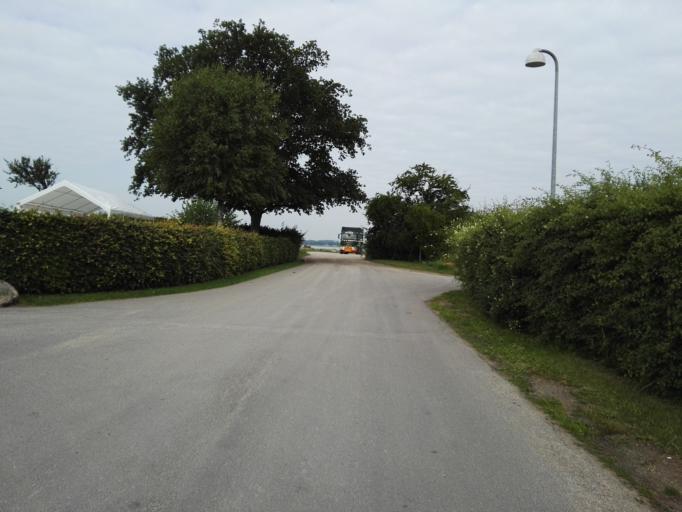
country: DK
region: Zealand
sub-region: Roskilde Kommune
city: Jyllinge
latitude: 55.7750
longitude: 12.0901
